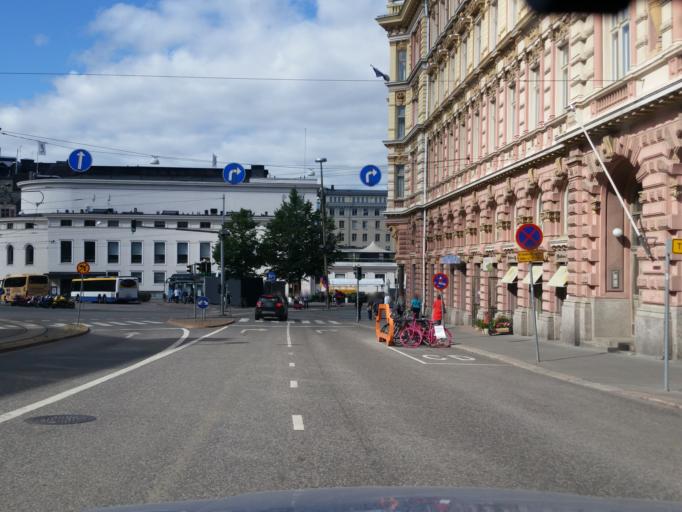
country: FI
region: Uusimaa
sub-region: Helsinki
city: Helsinki
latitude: 60.1661
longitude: 24.9439
